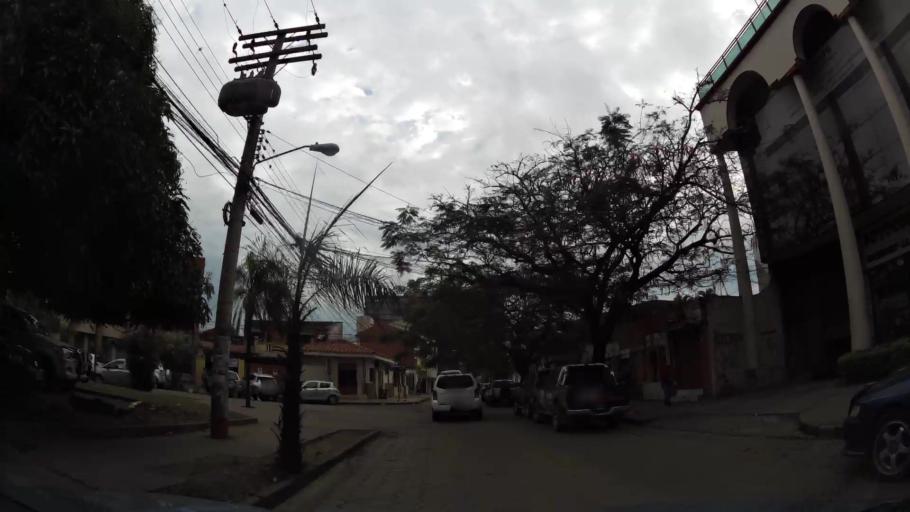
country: BO
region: Santa Cruz
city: Santa Cruz de la Sierra
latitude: -17.7737
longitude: -63.1807
